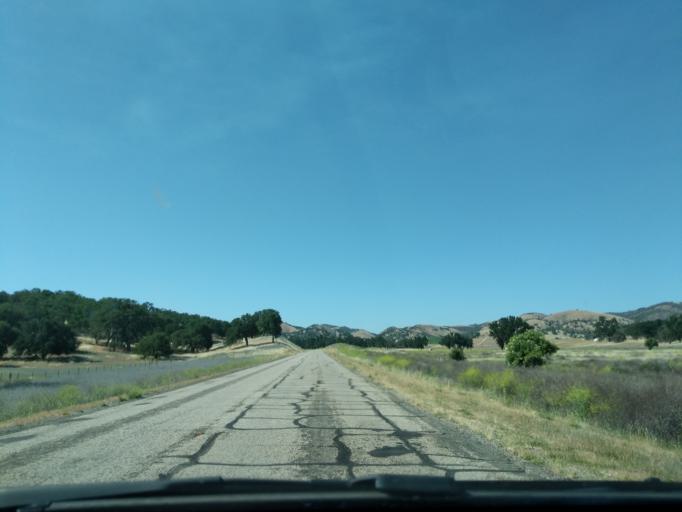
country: US
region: California
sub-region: Monterey County
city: King City
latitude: 36.0283
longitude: -121.1776
